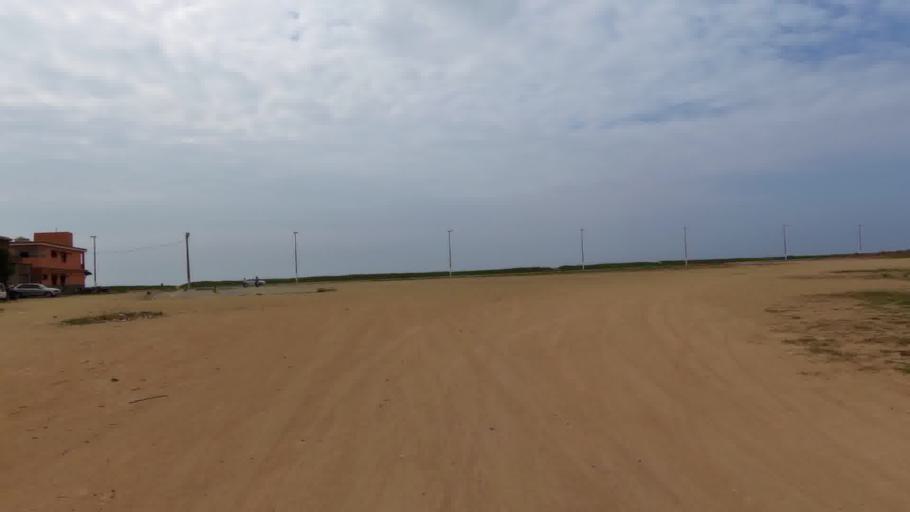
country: BR
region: Espirito Santo
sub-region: Marataizes
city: Marataizes
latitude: -21.0224
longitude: -40.8121
